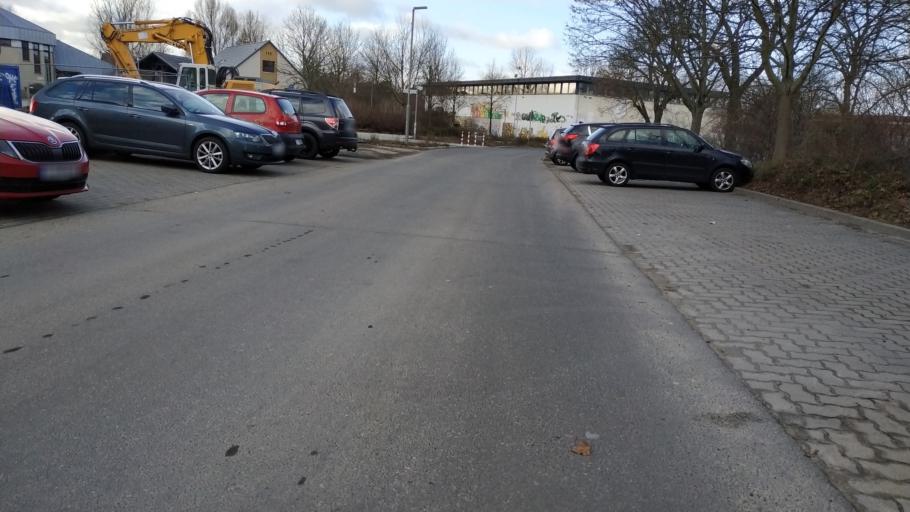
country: DE
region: Berlin
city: Hellersdorf
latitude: 52.5296
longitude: 13.6060
